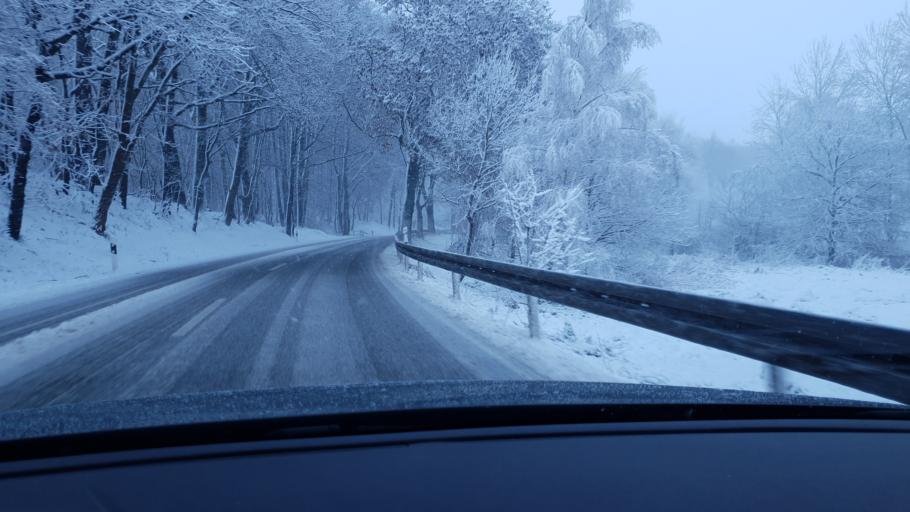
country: DE
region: Saxony
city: Claussnitz
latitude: 50.9178
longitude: 12.8758
